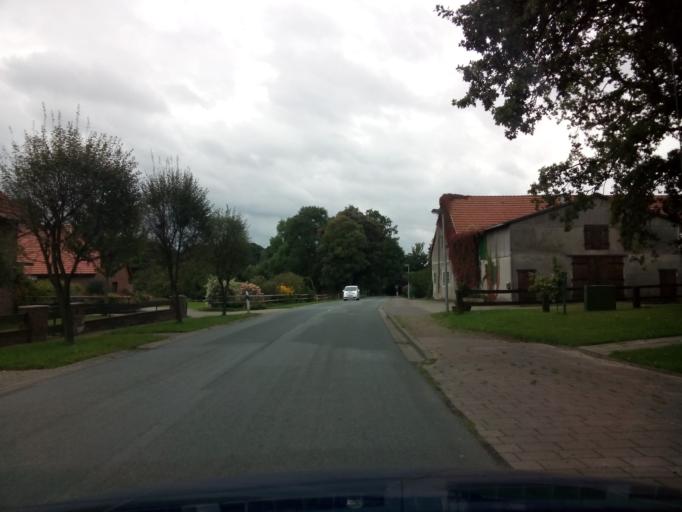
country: DE
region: Lower Saxony
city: Beverstedt
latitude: 53.4463
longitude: 8.8323
